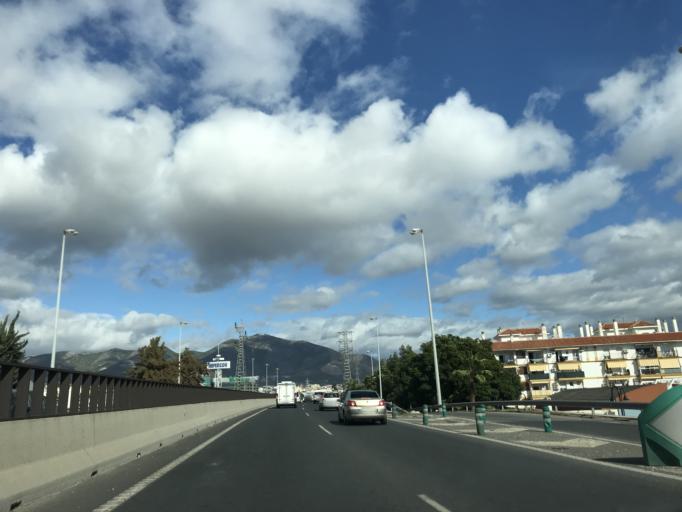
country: ES
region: Andalusia
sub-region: Provincia de Malaga
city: Fuengirola
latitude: 36.5443
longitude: -4.6339
